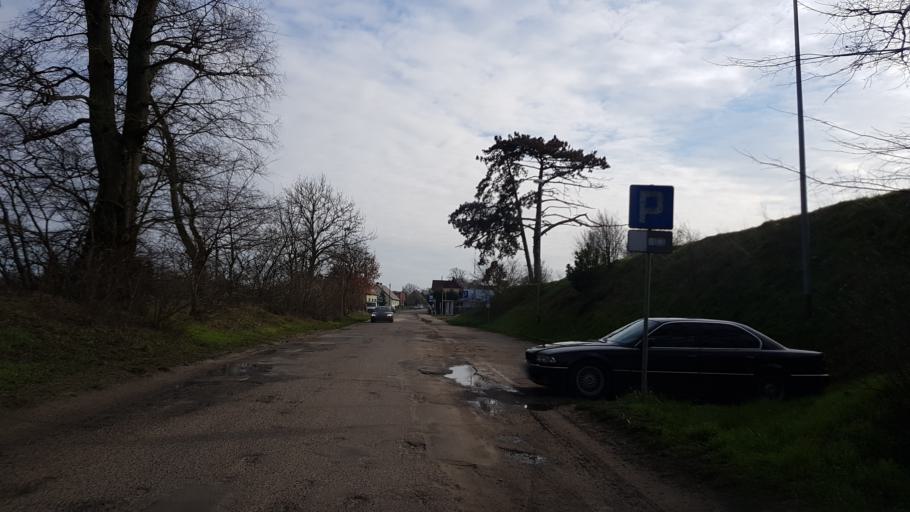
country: PL
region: West Pomeranian Voivodeship
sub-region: Powiat policki
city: Dobra
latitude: 53.5039
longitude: 14.3526
